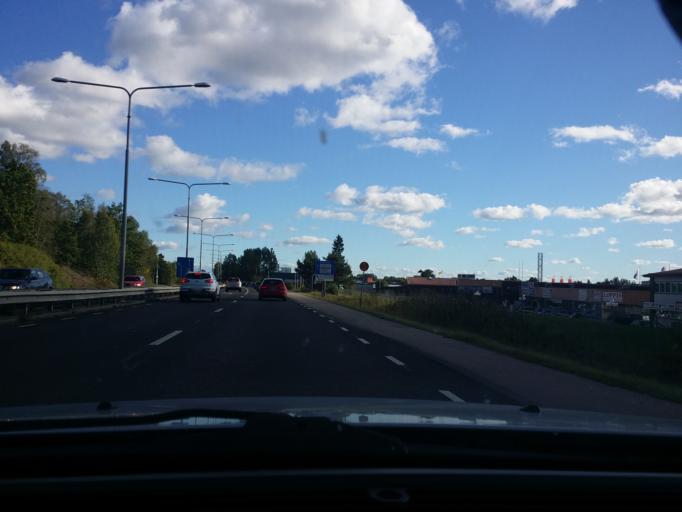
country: SE
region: Vaestmanland
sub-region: Vasteras
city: Vasteras
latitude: 59.6075
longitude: 16.4814
